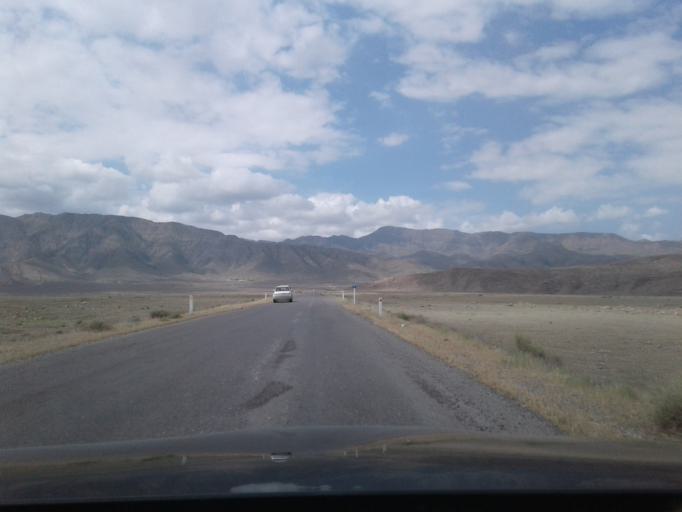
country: TM
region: Ahal
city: Baharly
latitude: 38.5172
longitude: 57.1363
